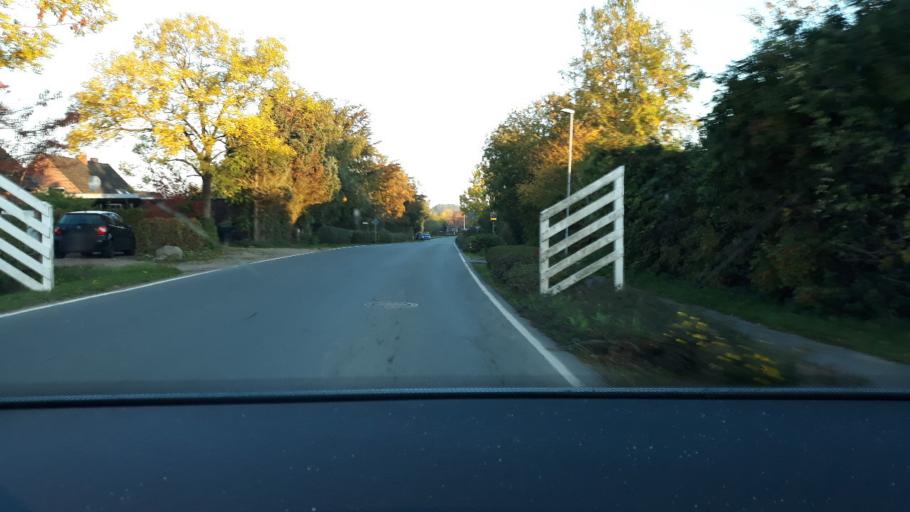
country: DE
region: Schleswig-Holstein
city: Satrup
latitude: 54.6770
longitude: 9.6040
